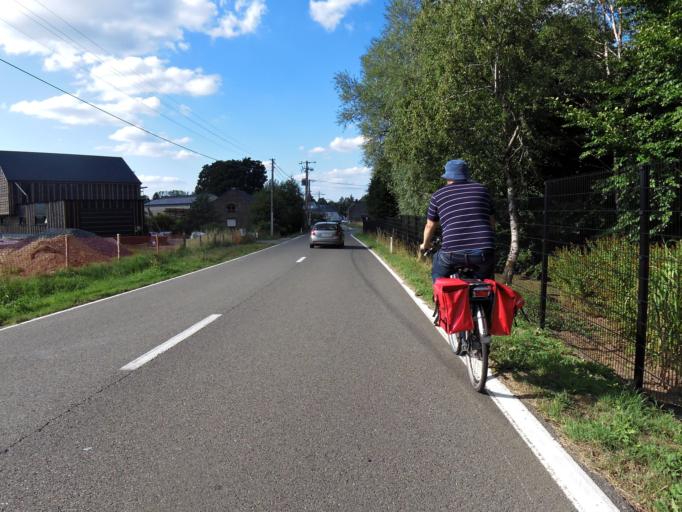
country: BE
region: Wallonia
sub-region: Province de Namur
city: Bievre
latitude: 49.9303
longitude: 5.0427
